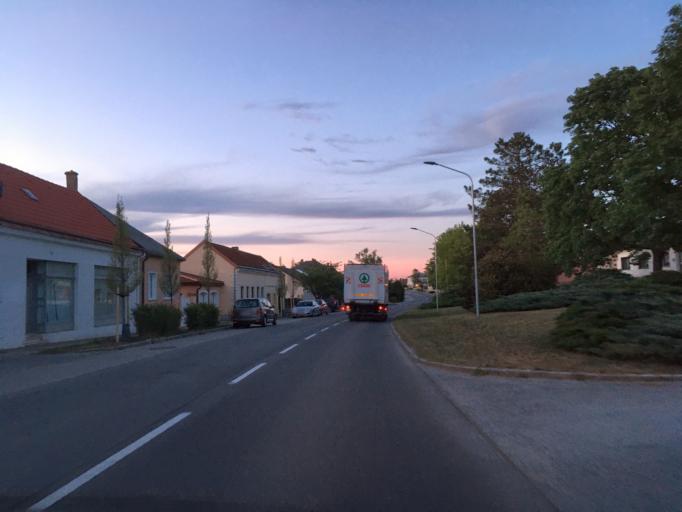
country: AT
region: Lower Austria
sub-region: Politischer Bezirk Wien-Umgebung
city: Zwolfaxing
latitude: 48.1117
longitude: 16.4634
